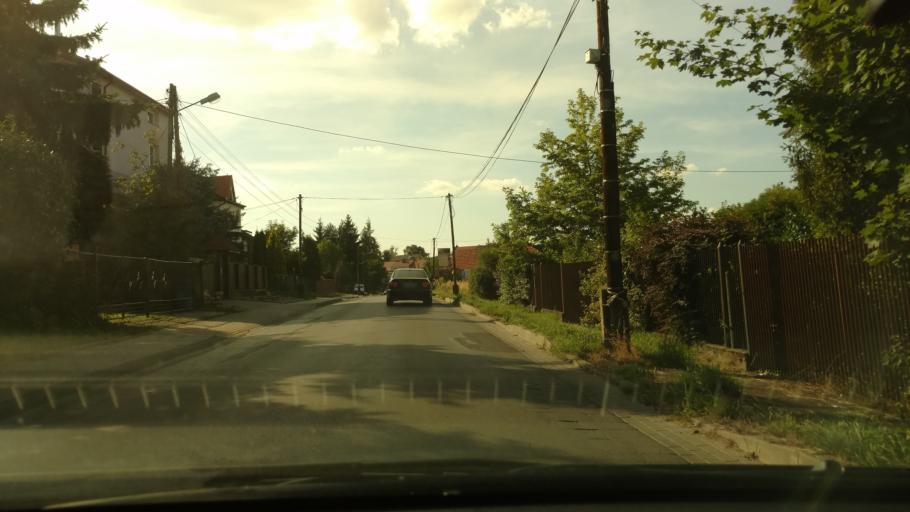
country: PL
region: Lesser Poland Voivodeship
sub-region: Powiat krakowski
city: Michalowice
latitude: 50.1154
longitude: 19.9723
